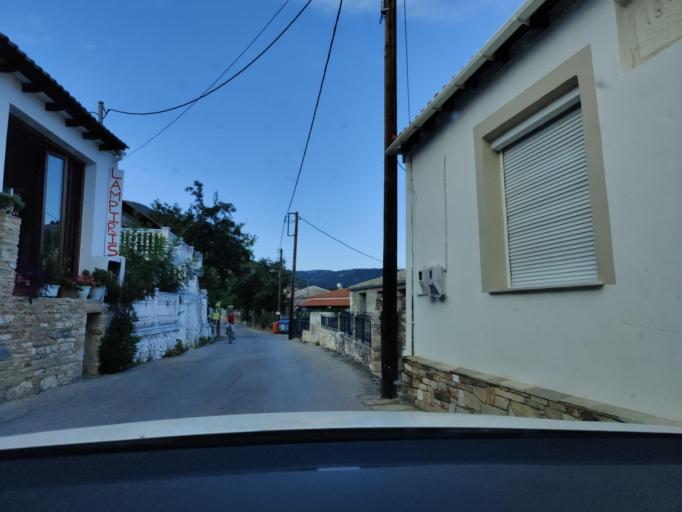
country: GR
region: East Macedonia and Thrace
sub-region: Nomos Kavalas
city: Potamia
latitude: 40.6573
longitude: 24.6891
